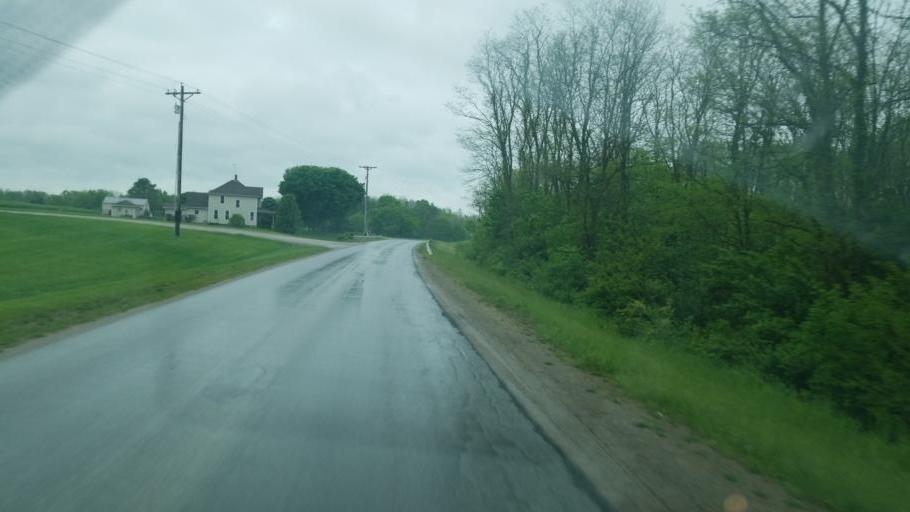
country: US
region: Ohio
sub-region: Highland County
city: Greenfield
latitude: 39.2945
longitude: -83.4630
